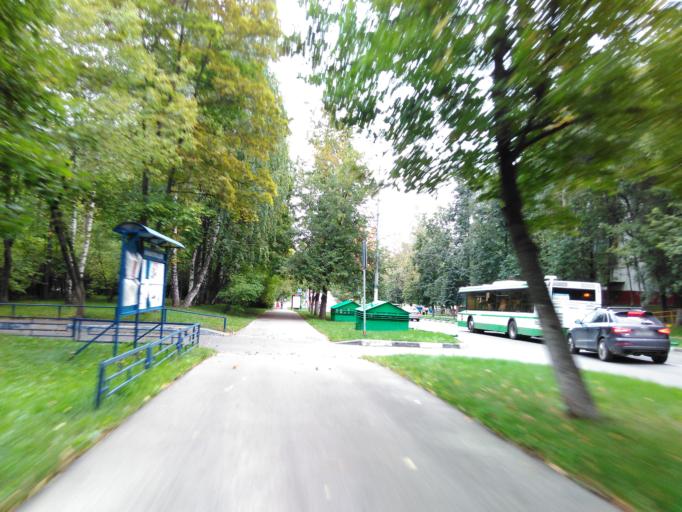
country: RU
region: Moscow
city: Kotlovka
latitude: 55.6613
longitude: 37.5867
